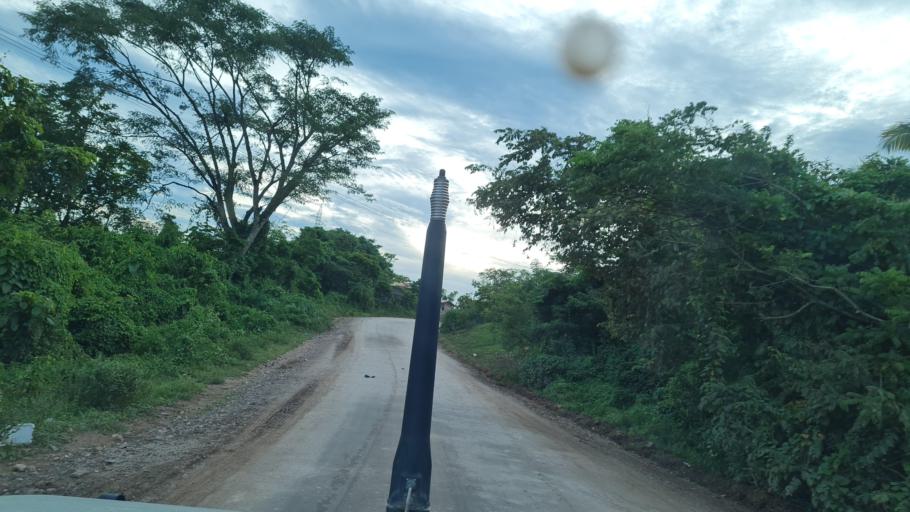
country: NI
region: Atlantico Norte (RAAN)
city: Siuna
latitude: 13.6860
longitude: -84.6159
